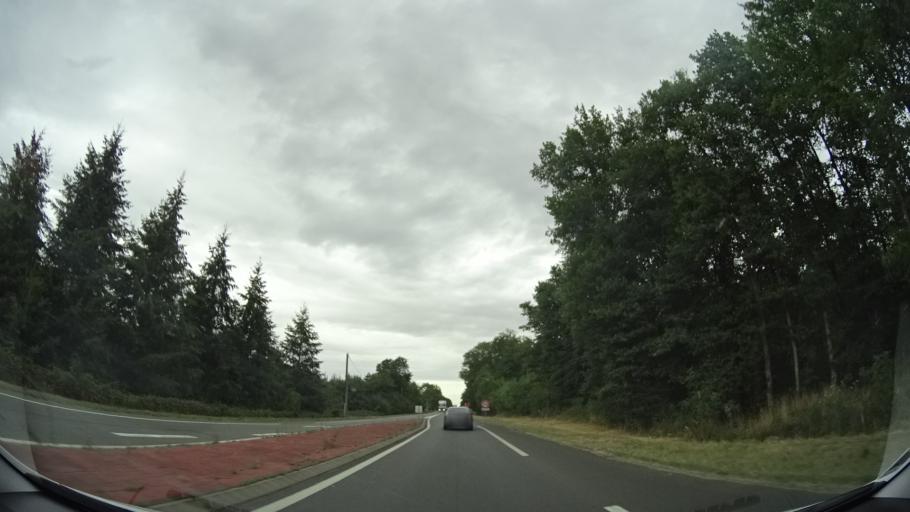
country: FR
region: Centre
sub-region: Departement du Loiret
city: Vitry-aux-Loges
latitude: 47.9361
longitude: 2.3487
